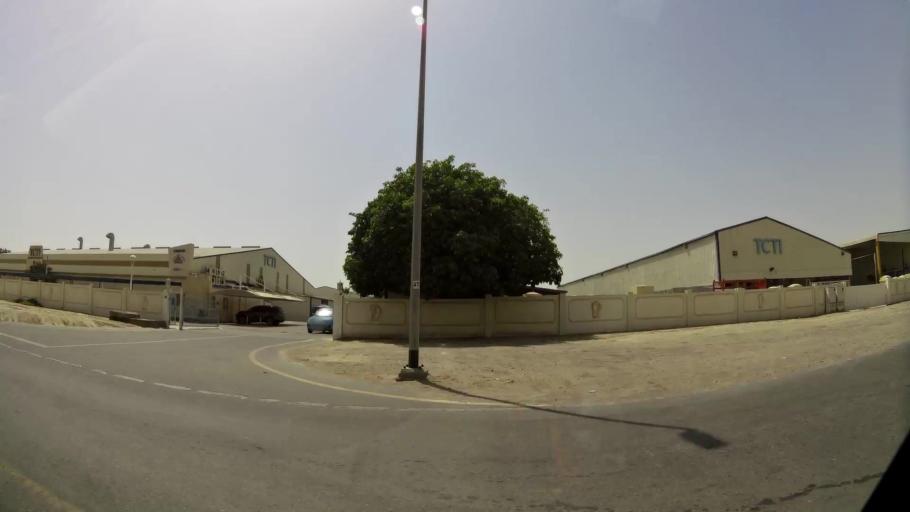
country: AE
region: Dubai
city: Dubai
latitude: 25.1467
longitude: 55.2401
